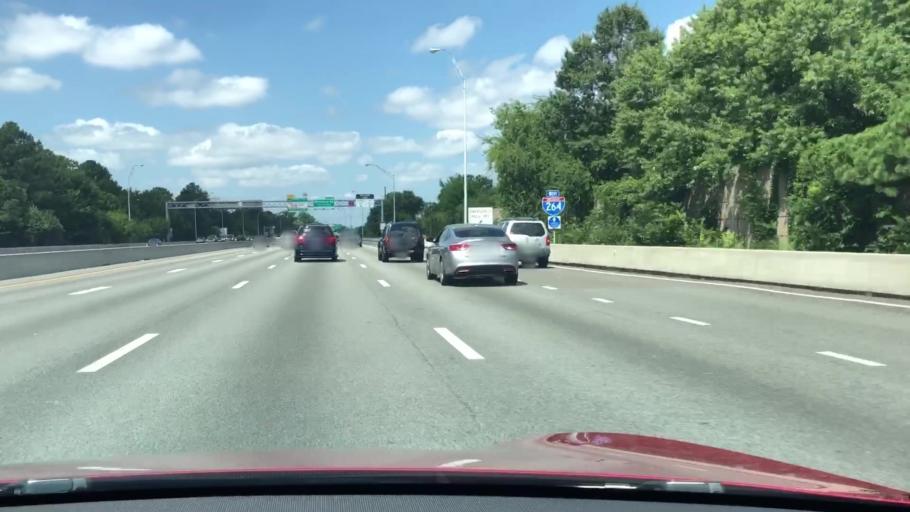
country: US
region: Virginia
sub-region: City of Chesapeake
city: Chesapeake
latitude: 36.8353
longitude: -76.1459
